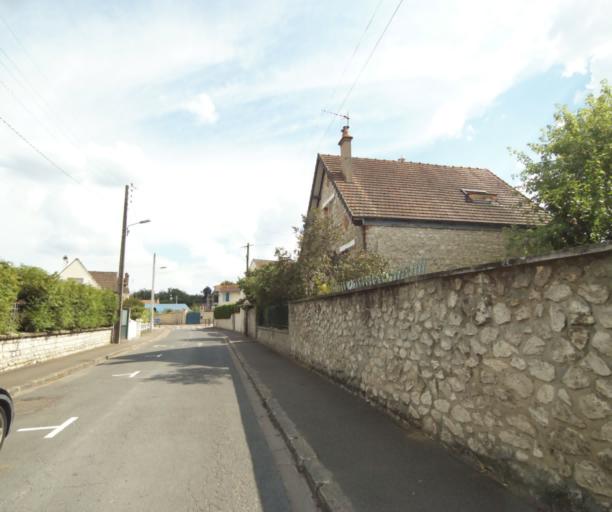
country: FR
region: Ile-de-France
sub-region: Departement de Seine-et-Marne
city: Avon
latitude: 48.4033
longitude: 2.7253
